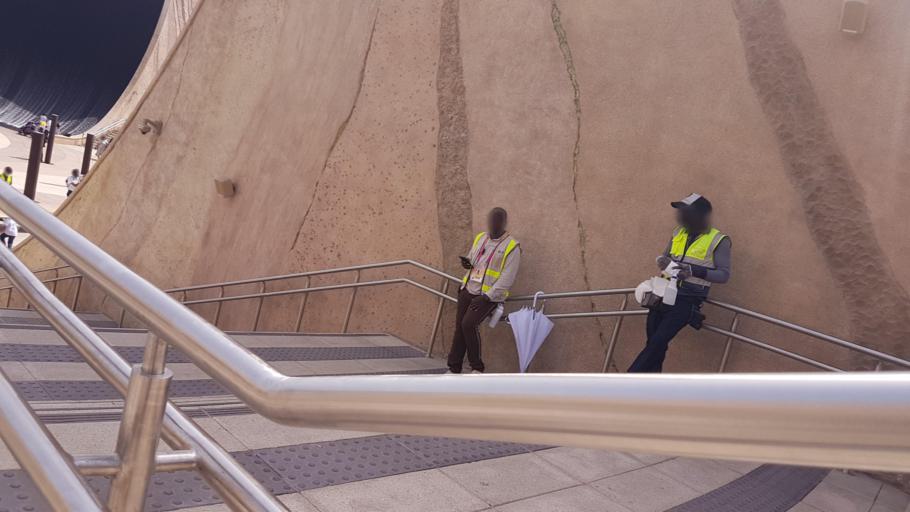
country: AE
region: Dubai
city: Dubai
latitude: 24.9589
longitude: 55.1507
